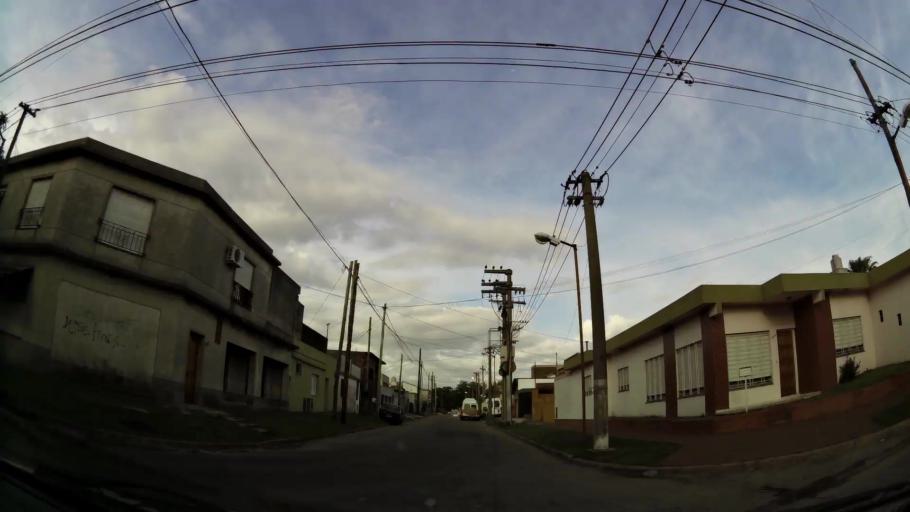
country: AR
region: Buenos Aires
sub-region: Partido de Quilmes
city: Quilmes
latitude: -34.7357
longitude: -58.2646
